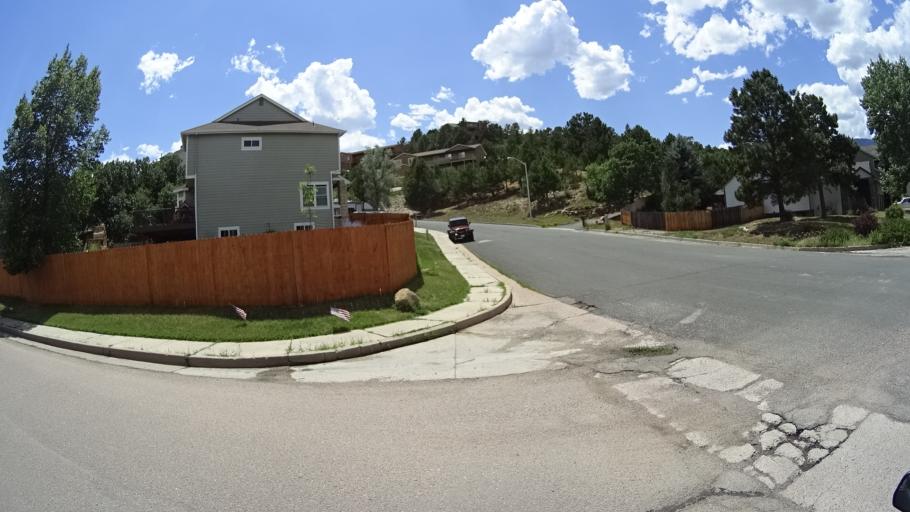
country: US
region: Colorado
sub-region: El Paso County
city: Air Force Academy
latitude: 38.9405
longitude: -104.8429
